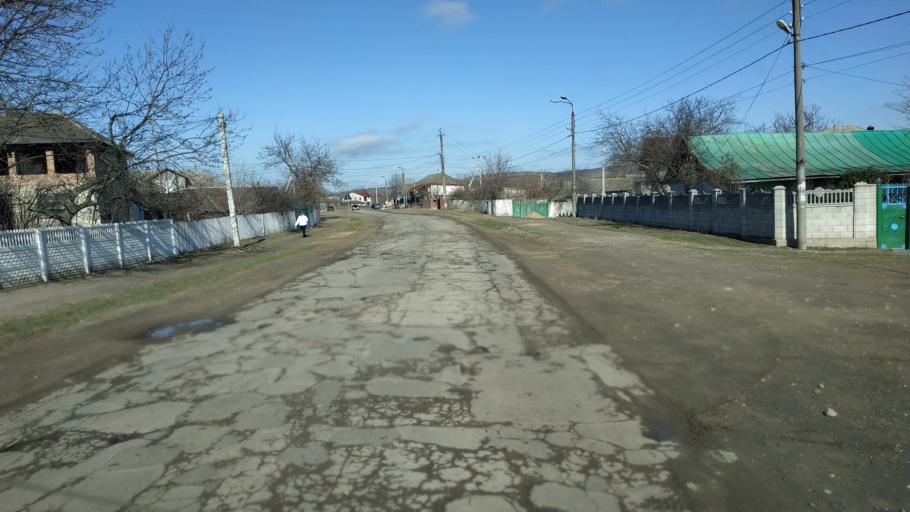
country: MD
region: Hincesti
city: Hincesti
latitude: 46.9613
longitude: 28.6028
